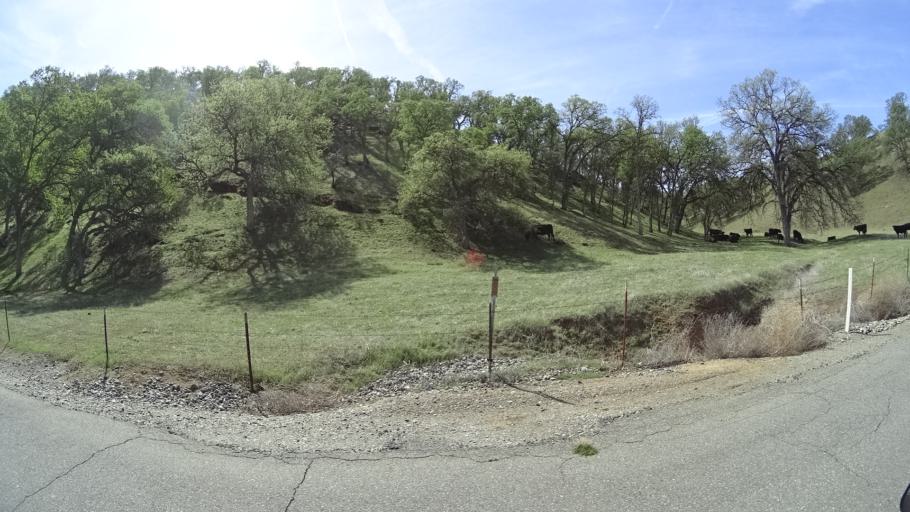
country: US
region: California
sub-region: Glenn County
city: Willows
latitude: 39.5442
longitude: -122.4052
